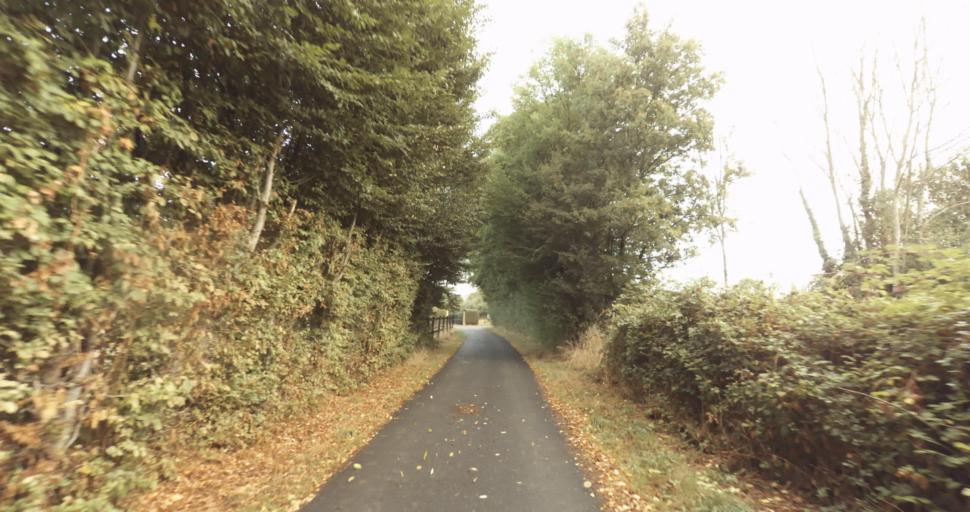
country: FR
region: Lower Normandy
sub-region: Departement de l'Orne
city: Vimoutiers
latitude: 48.9016
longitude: 0.2483
